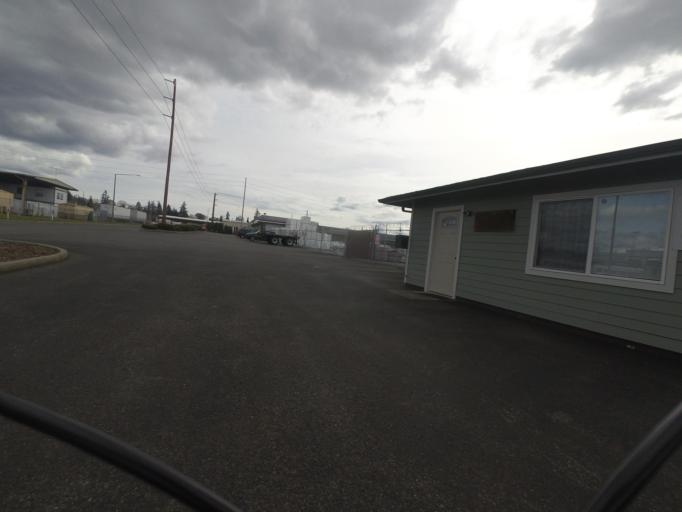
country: US
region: Washington
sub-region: Pierce County
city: Lakewood
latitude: 47.1715
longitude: -122.4902
